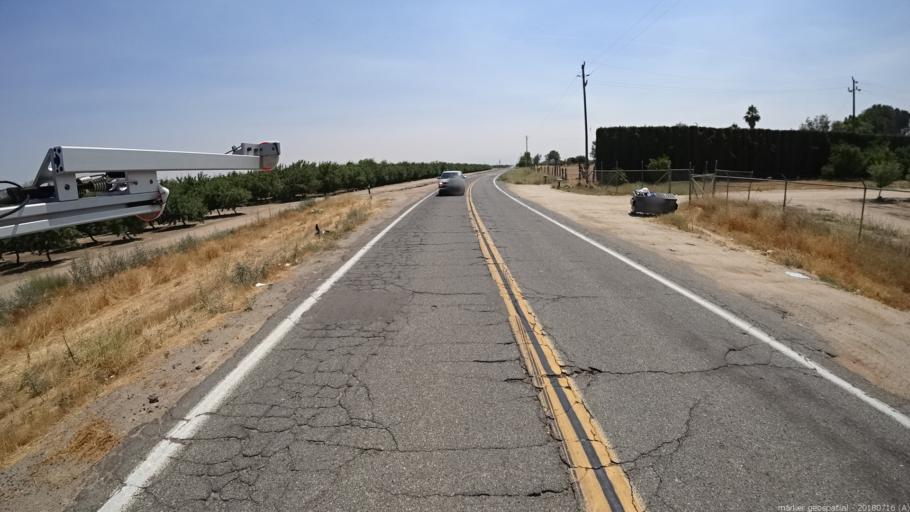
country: US
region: California
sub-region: Madera County
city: Madera Acres
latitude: 37.0544
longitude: -120.0885
